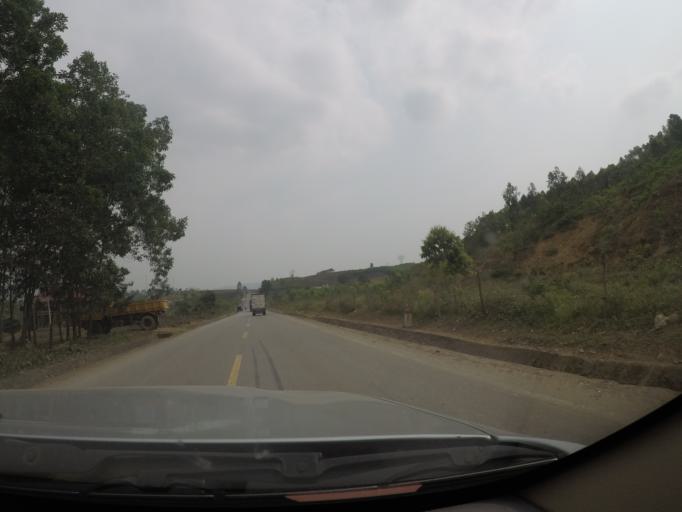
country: VN
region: Thanh Hoa
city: Thi Tran Ben Sung
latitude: 19.3878
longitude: 105.4580
